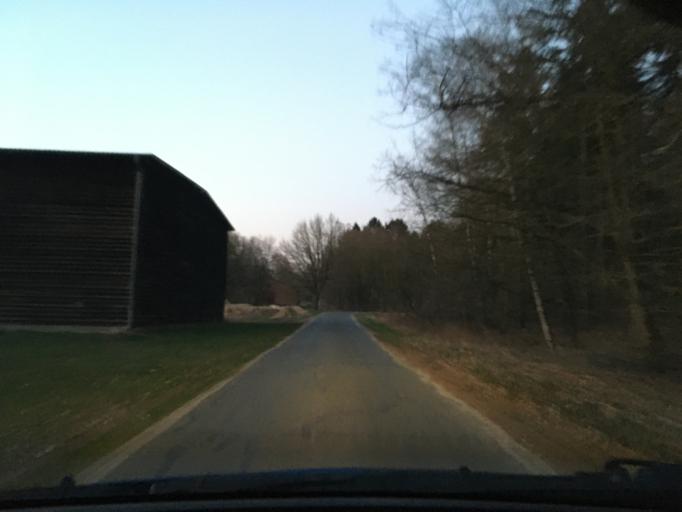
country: DE
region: Lower Saxony
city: Rehlingen
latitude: 53.0635
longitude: 10.2375
